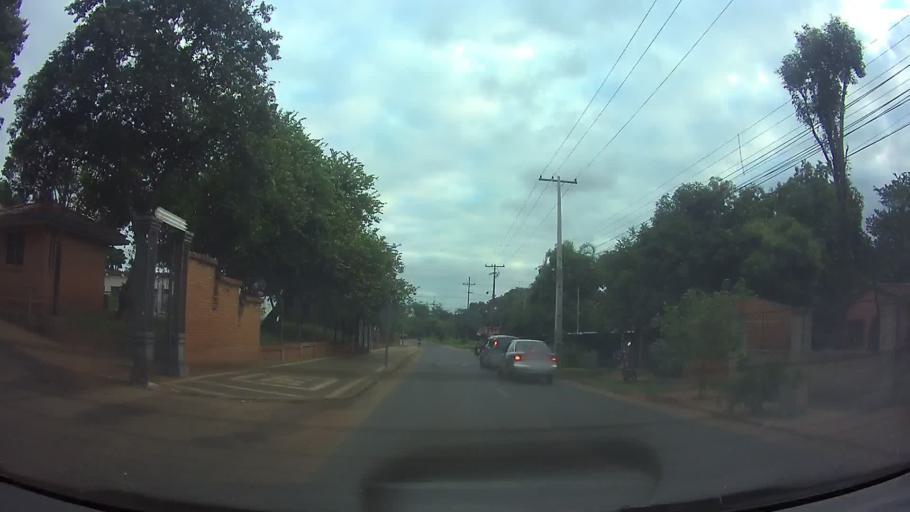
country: PY
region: Central
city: San Lorenzo
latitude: -25.2953
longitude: -57.4917
